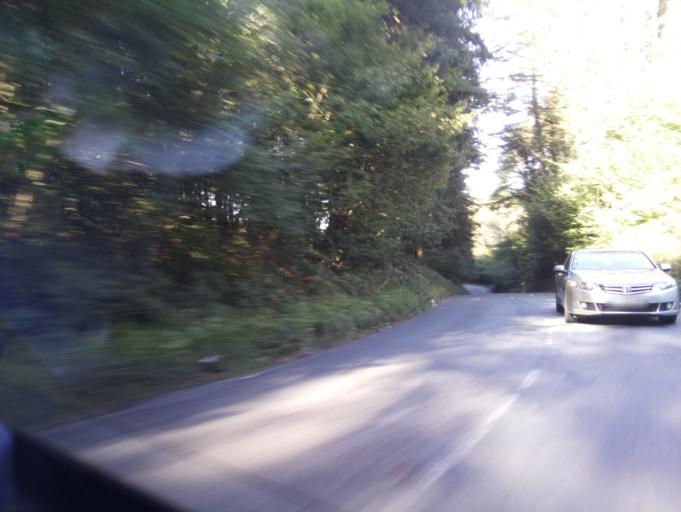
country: GB
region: Wales
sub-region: Newport
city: Newport
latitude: 51.6055
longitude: -3.0475
